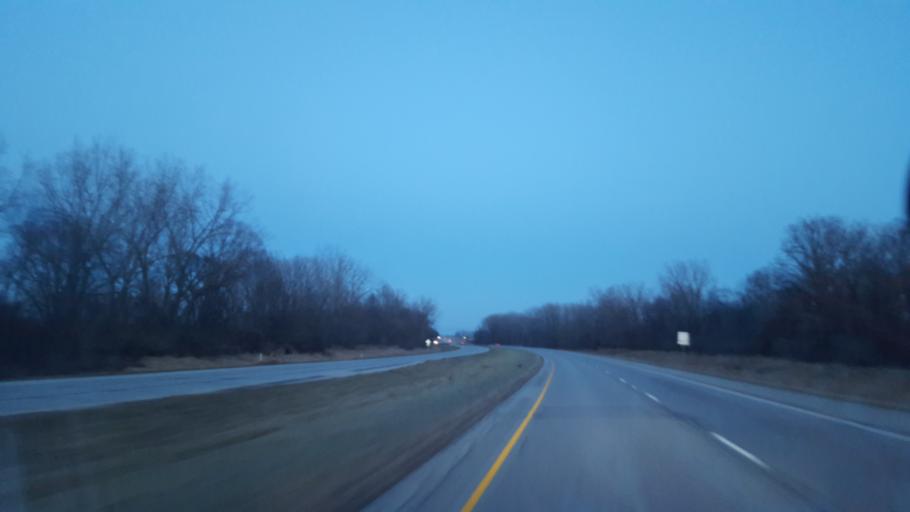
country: US
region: Indiana
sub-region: Kosciusko County
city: Mentone
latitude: 41.2649
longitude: -85.9675
